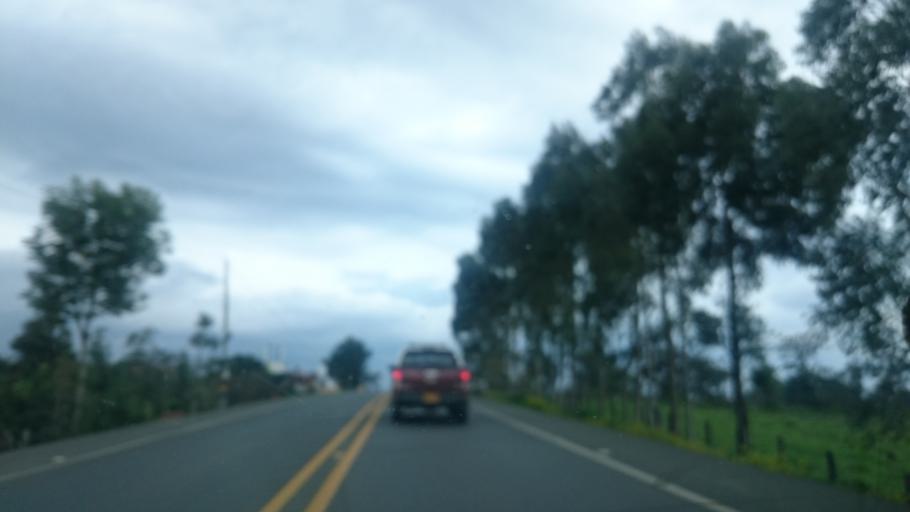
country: CO
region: Cauca
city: Cajibio
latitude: 2.5859
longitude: -76.5378
